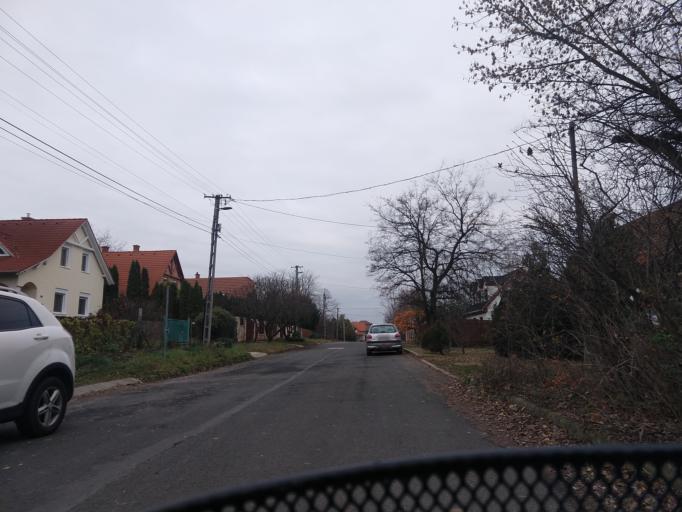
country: HU
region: Pest
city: Orbottyan
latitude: 47.6739
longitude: 19.2854
